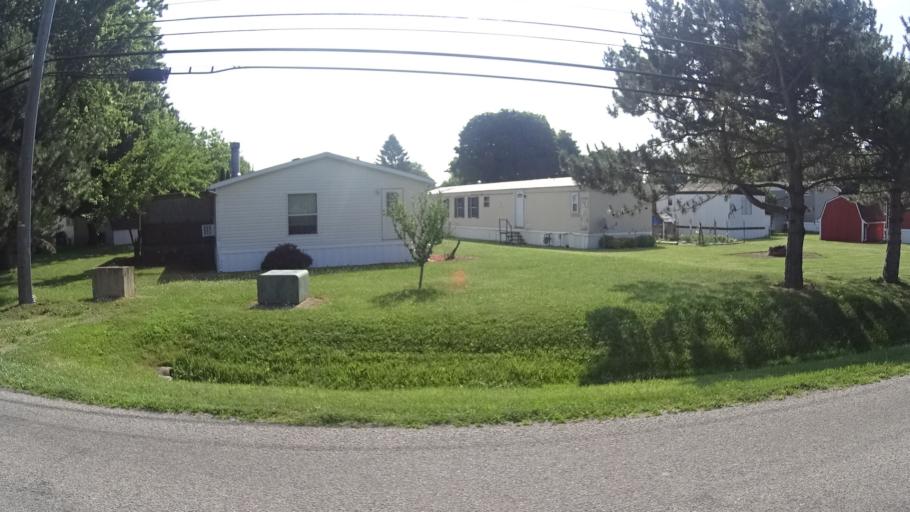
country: US
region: Ohio
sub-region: Lorain County
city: Vermilion
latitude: 41.3953
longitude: -82.4306
